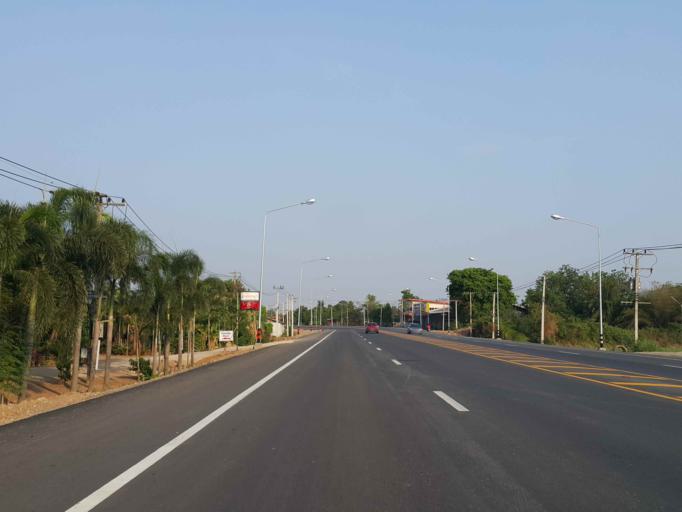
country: TH
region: Sukhothai
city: Sawankhalok
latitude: 17.3043
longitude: 99.8222
